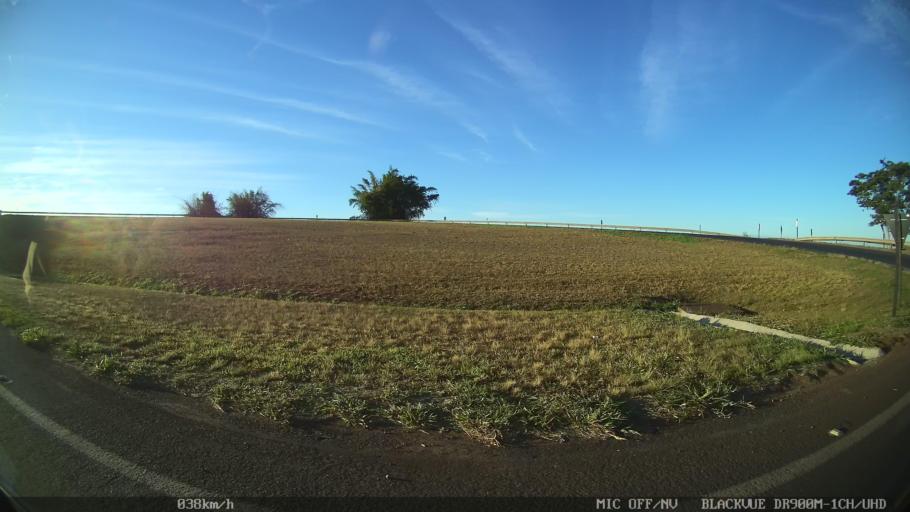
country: BR
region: Sao Paulo
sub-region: Catanduva
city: Catanduva
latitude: -21.0495
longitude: -49.1288
